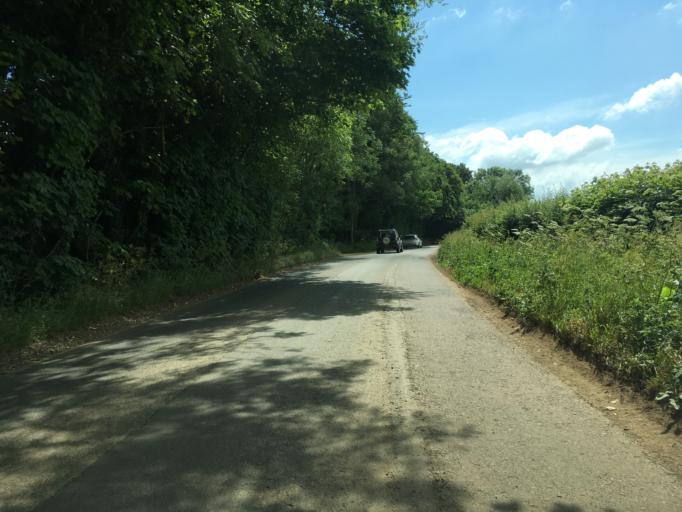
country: GB
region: England
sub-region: Gloucestershire
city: Coates
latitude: 51.7279
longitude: -2.0646
